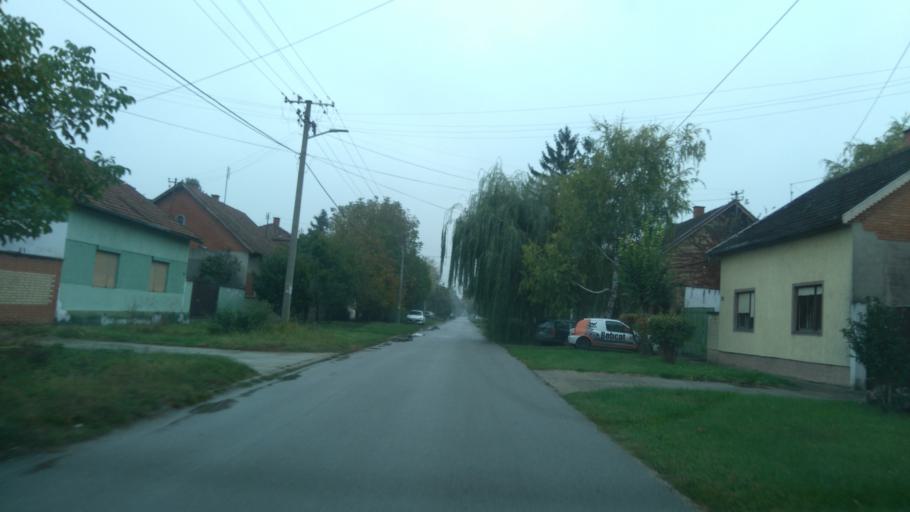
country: RS
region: Autonomna Pokrajina Vojvodina
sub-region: Juznobacki Okrug
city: Becej
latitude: 45.6138
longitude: 20.0405
